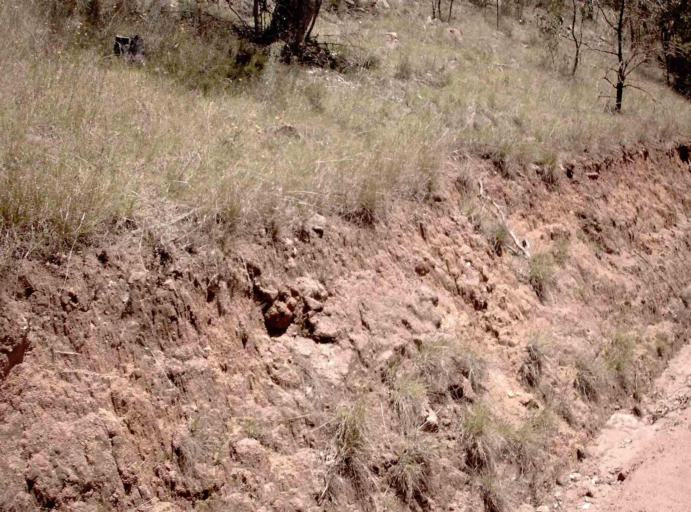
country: AU
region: New South Wales
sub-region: Snowy River
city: Jindabyne
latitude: -36.9327
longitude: 148.3556
